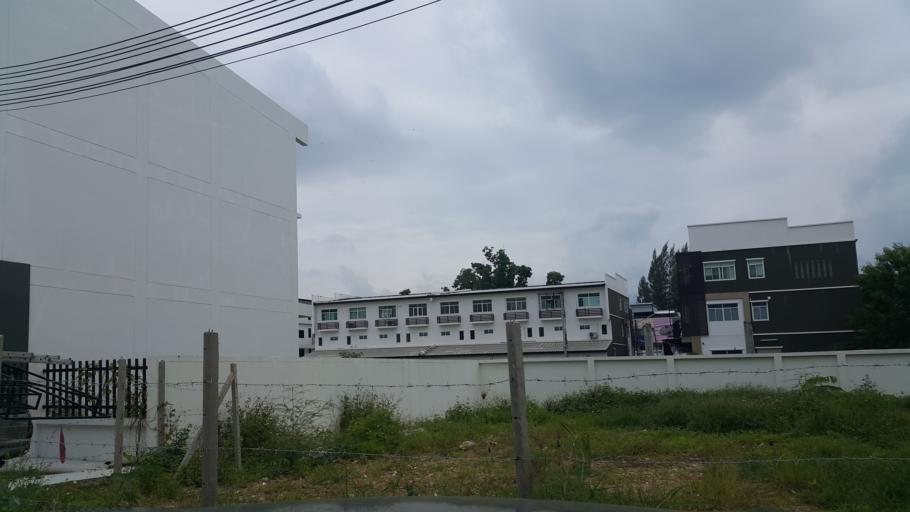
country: TH
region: Chiang Mai
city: San Sai
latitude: 18.8299
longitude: 99.0137
